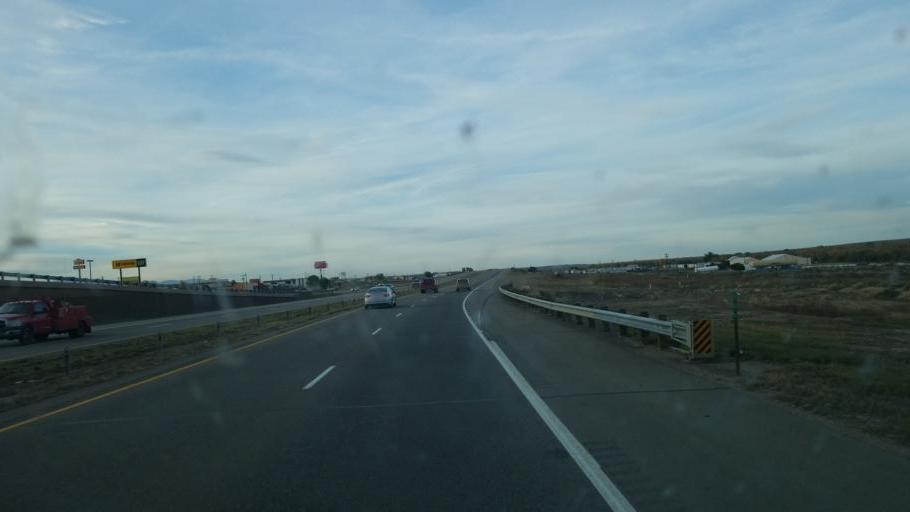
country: US
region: Colorado
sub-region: Pueblo County
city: Pueblo
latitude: 38.3383
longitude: -104.6199
